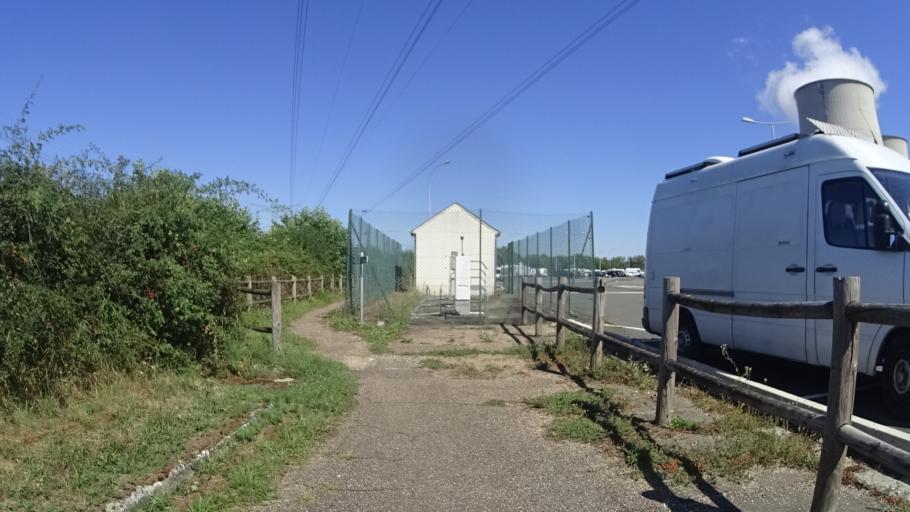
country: FR
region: Centre
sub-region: Departement du Cher
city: Belleville-sur-Loire
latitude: 47.5081
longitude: 2.8677
